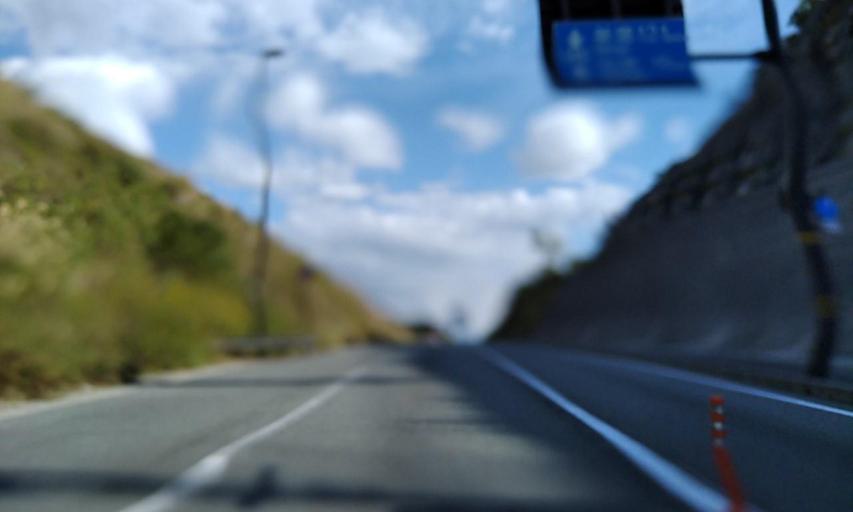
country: JP
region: Wakayama
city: Tanabe
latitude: 33.7500
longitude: 135.3586
